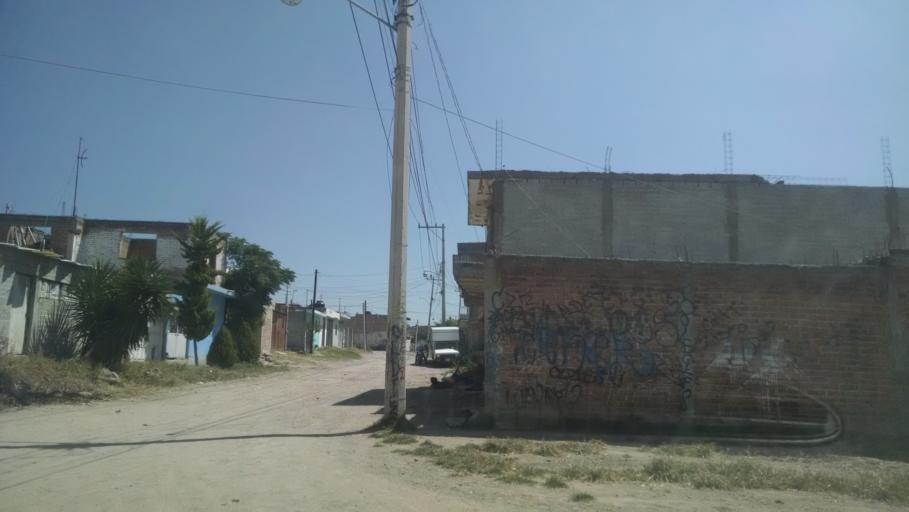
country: MX
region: Guanajuato
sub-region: Leon
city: La Ermita
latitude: 21.1491
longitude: -101.7350
